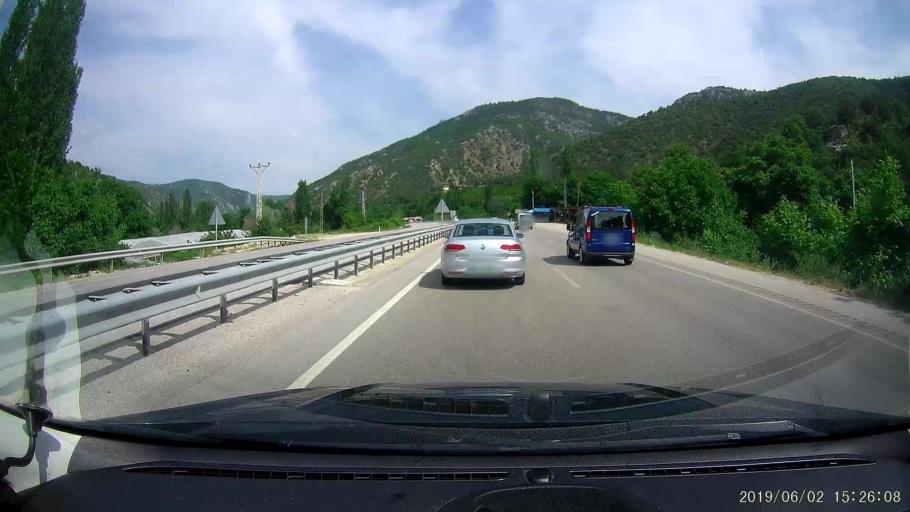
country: TR
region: Amasya
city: Saraycik
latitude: 40.9878
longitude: 35.0312
